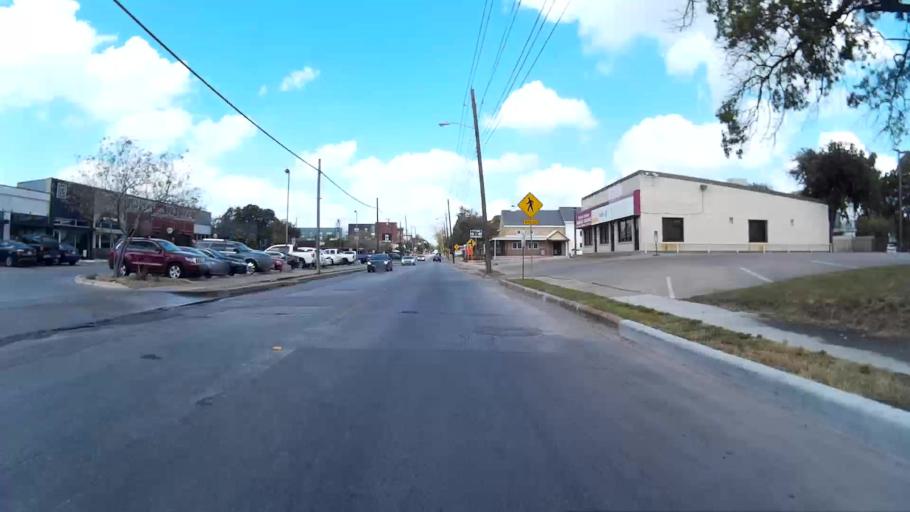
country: US
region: Texas
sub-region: Dallas County
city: Highland Park
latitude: 32.8141
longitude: -96.7776
